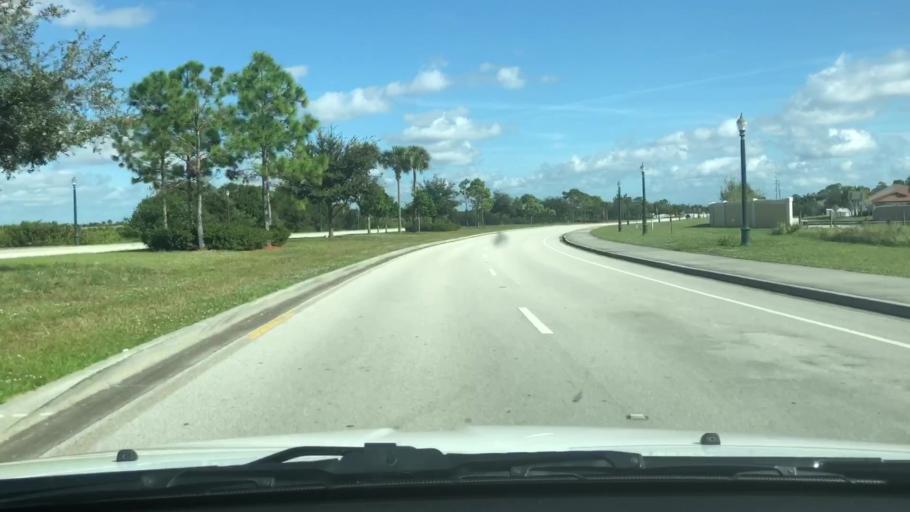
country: US
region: Florida
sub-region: Saint Lucie County
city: Port Saint Lucie
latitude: 27.2942
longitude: -80.4327
